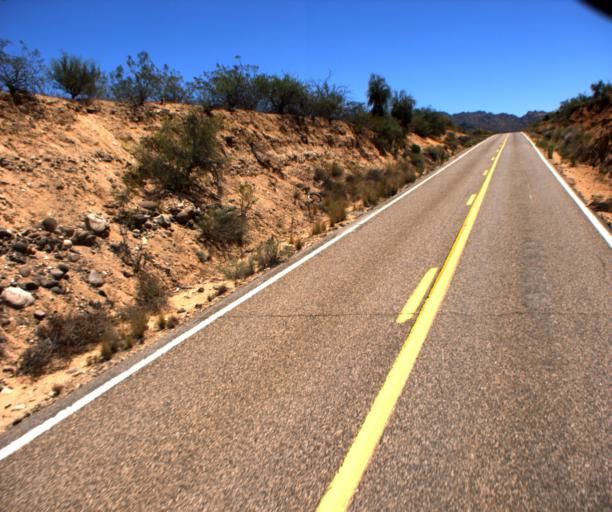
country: US
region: Arizona
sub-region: Yavapai County
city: Bagdad
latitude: 34.4780
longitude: -113.0580
